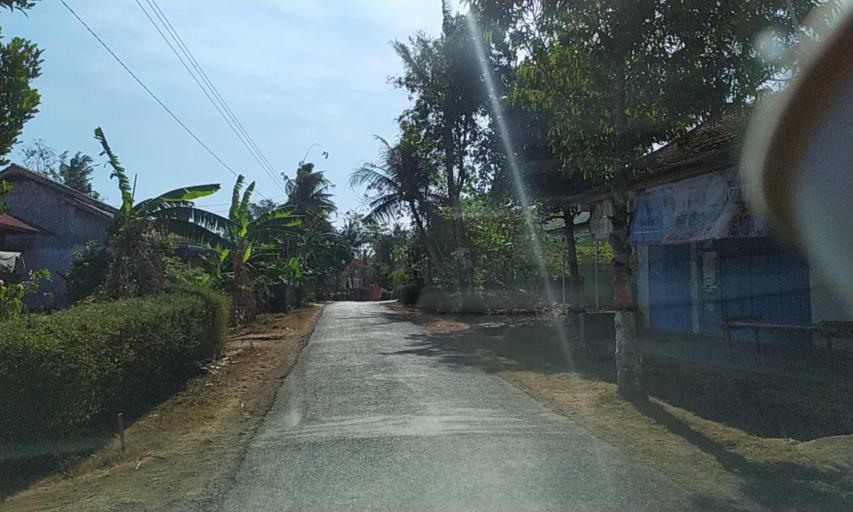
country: ID
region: Central Java
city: Kroya
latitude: -7.6460
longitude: 109.2986
